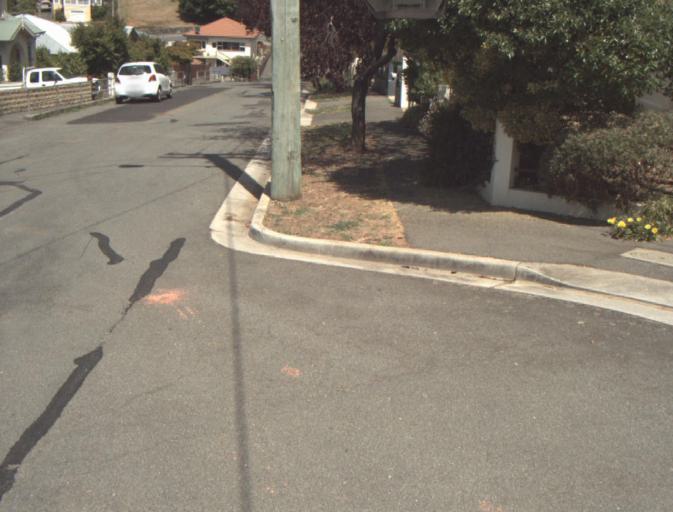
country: AU
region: Tasmania
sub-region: Launceston
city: West Launceston
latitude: -41.4500
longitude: 147.1366
